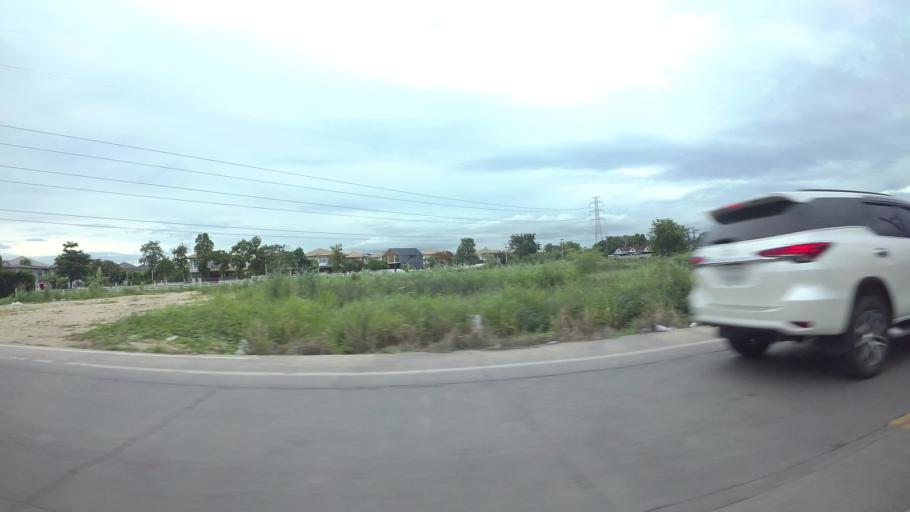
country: TH
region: Chon Buri
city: Si Racha
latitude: 13.1409
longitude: 100.9621
